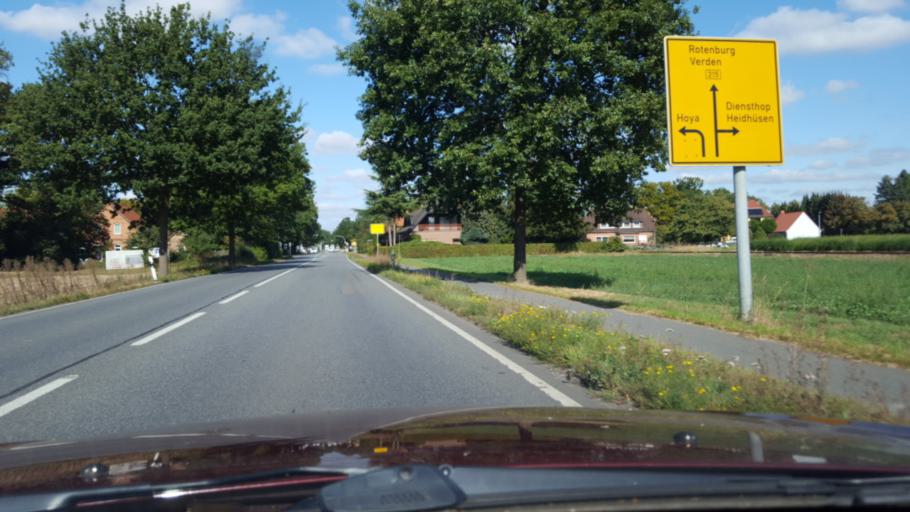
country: DE
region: Lower Saxony
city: Eystrup
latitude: 52.8002
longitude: 9.2091
